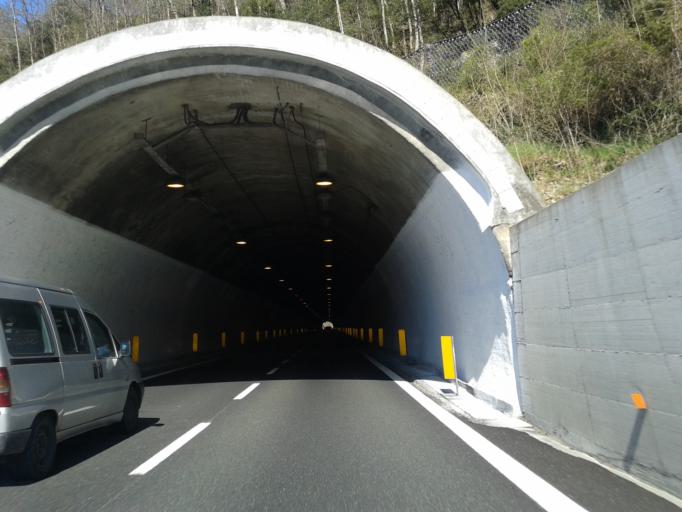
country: IT
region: Liguria
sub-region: Provincia di La Spezia
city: Padivarma
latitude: 44.2157
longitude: 9.7633
